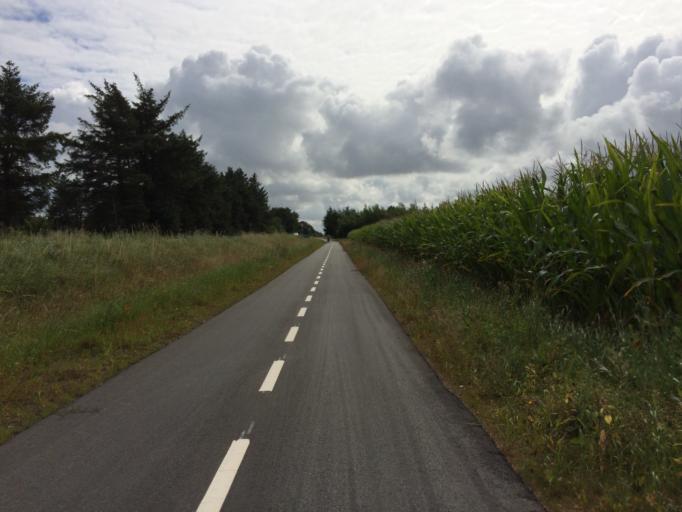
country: DK
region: Central Jutland
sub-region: Holstebro Kommune
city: Ulfborg
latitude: 56.3040
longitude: 8.3385
